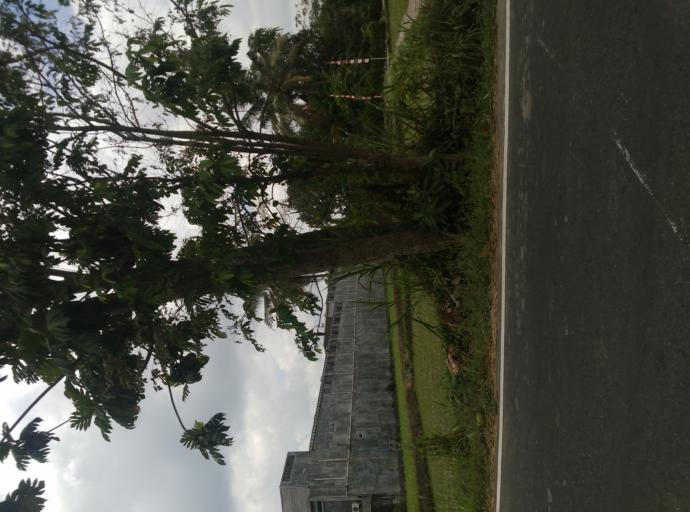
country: ID
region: Daerah Istimewa Yogyakarta
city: Depok
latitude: -7.7194
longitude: 110.4382
